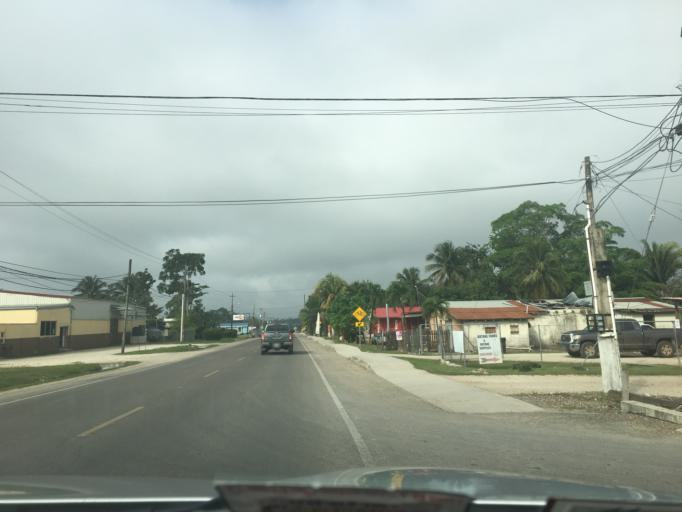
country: BZ
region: Cayo
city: Belmopan
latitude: 17.2494
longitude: -88.7786
